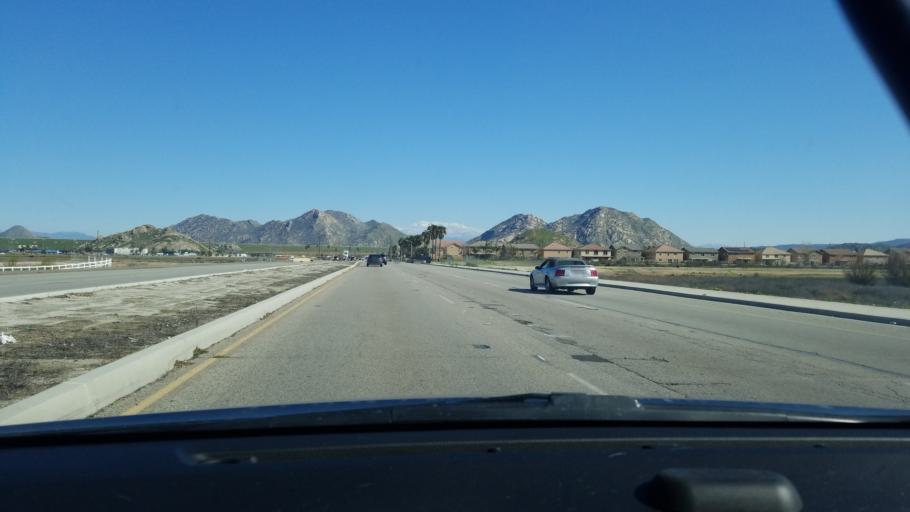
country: US
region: California
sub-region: Riverside County
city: Perris
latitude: 33.8445
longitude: -117.2150
